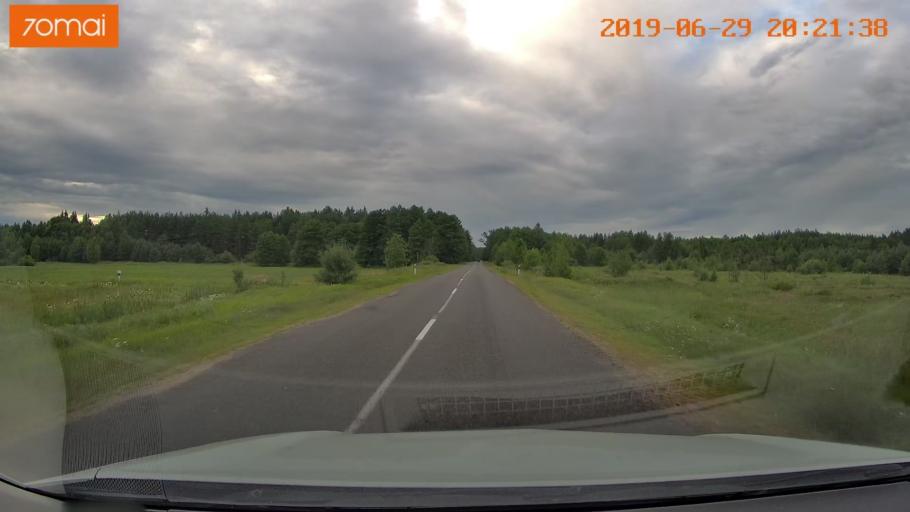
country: BY
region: Brest
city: Asnyezhytsy
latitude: 52.4221
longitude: 26.2531
